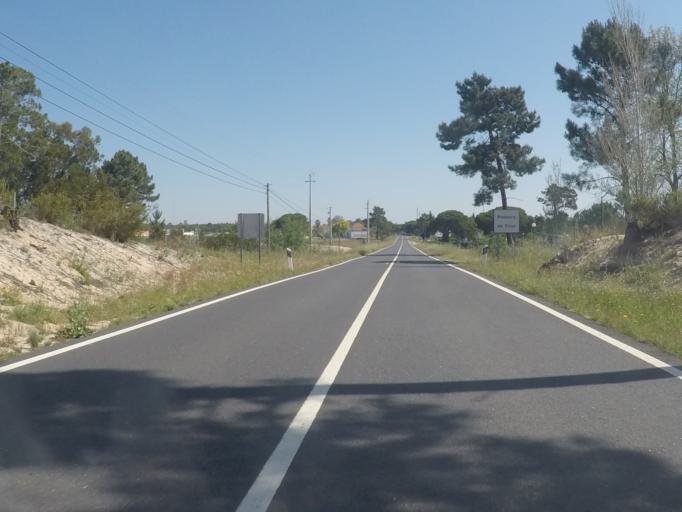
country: PT
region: Setubal
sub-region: Grandola
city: Grandola
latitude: 38.2638
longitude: -8.7299
